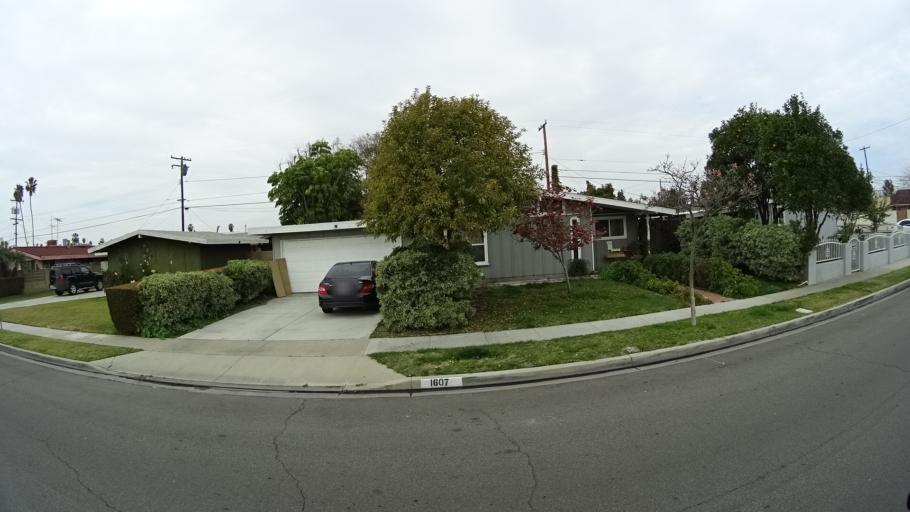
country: US
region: California
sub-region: Orange County
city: Anaheim
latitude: 33.8448
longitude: -117.9403
